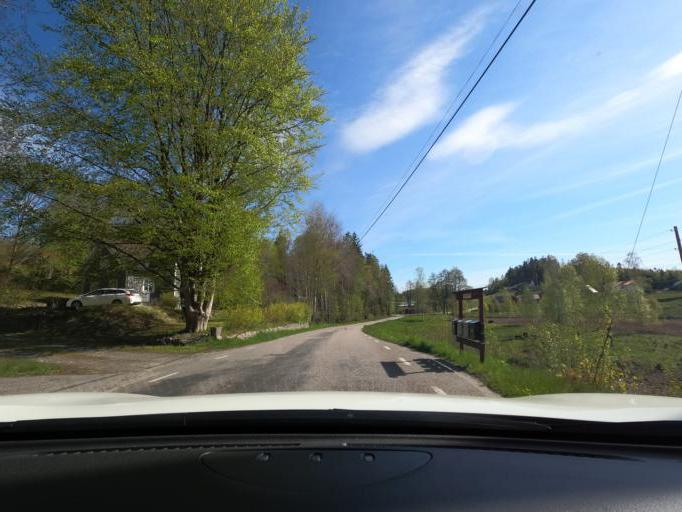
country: SE
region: Vaestra Goetaland
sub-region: Harryda Kommun
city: Hindas
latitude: 57.6422
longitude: 12.3516
